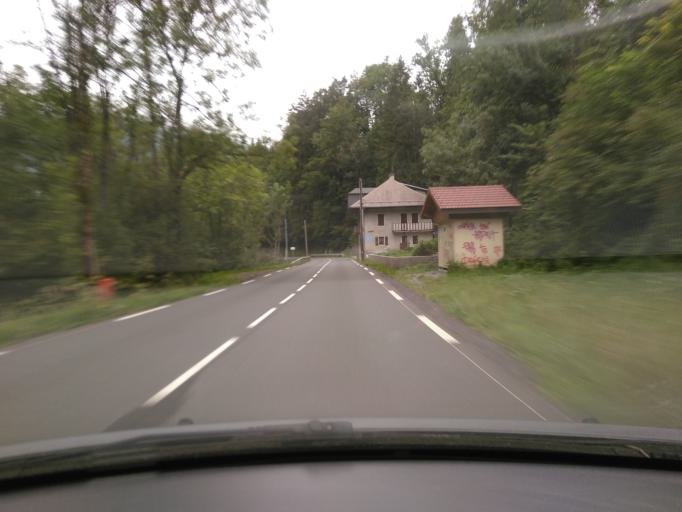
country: FR
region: Rhone-Alpes
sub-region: Departement de la Haute-Savoie
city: Saint-Jean-de-Sixt
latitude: 45.9492
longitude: 6.3975
